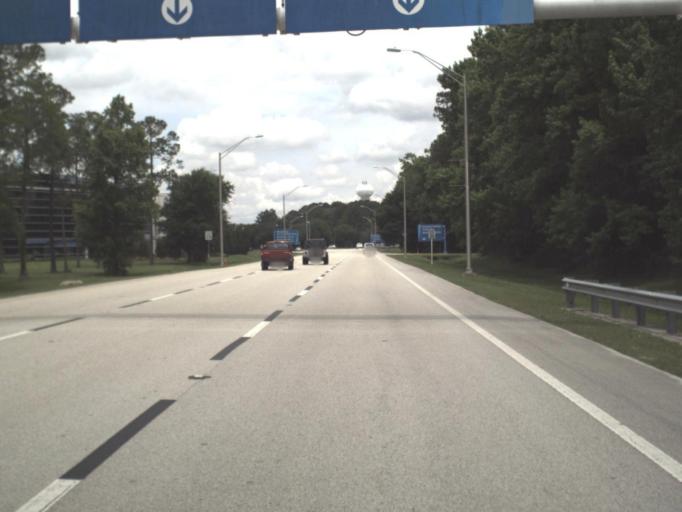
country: US
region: Florida
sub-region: Nassau County
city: Nassau Village-Ratliff
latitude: 30.4883
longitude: -81.6715
